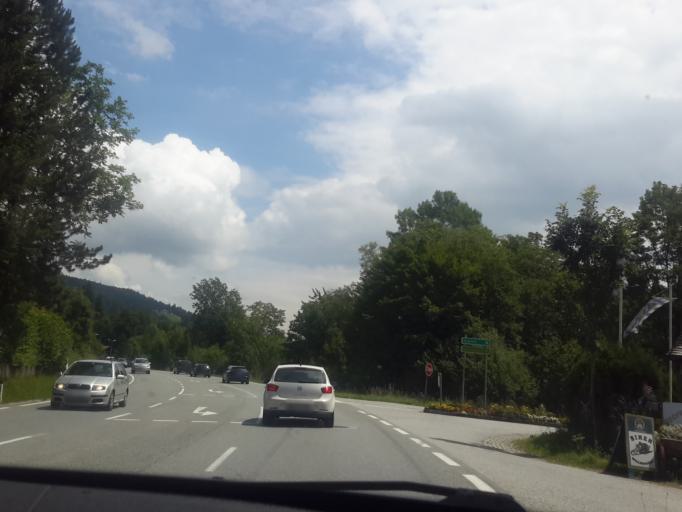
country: AT
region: Tyrol
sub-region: Politischer Bezirk Kufstein
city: Ellmau
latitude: 47.5210
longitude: 12.2761
